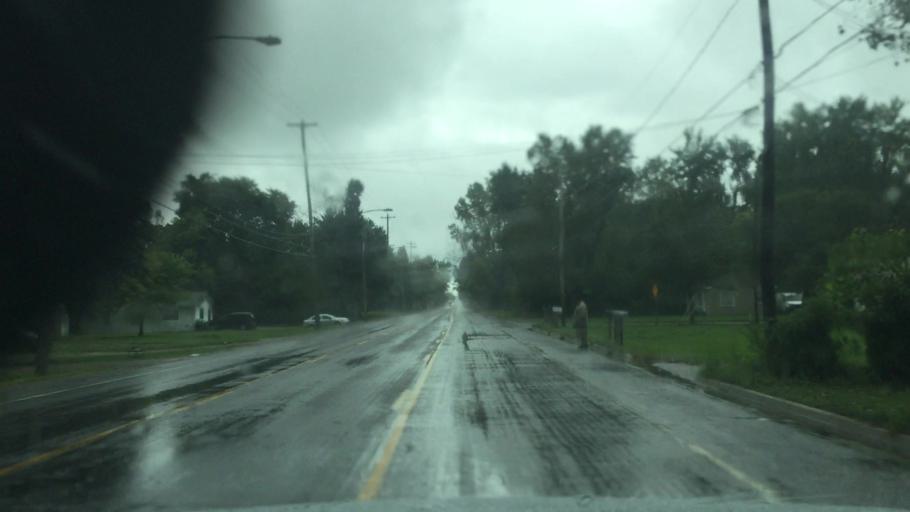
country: US
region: Michigan
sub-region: Eaton County
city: Dimondale
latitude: 42.6798
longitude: -84.6031
